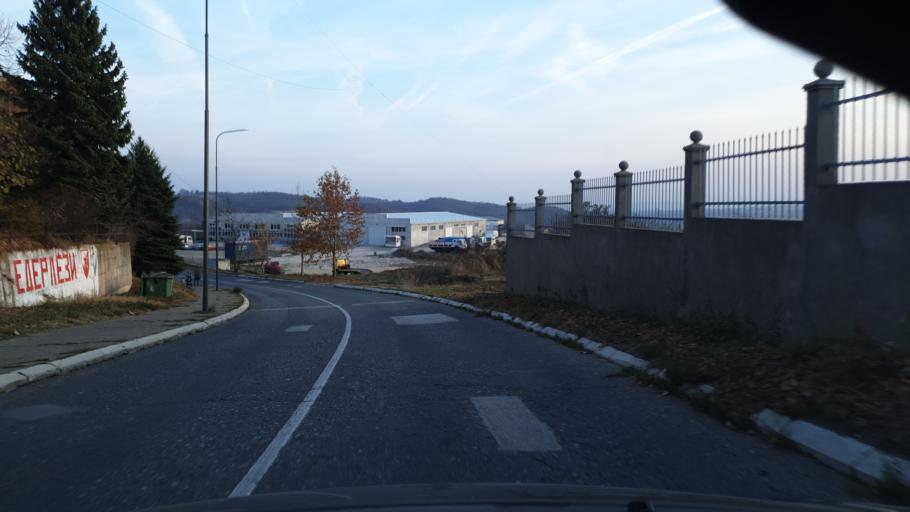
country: RS
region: Central Serbia
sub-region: Borski Okrug
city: Bor
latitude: 44.0549
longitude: 22.0957
